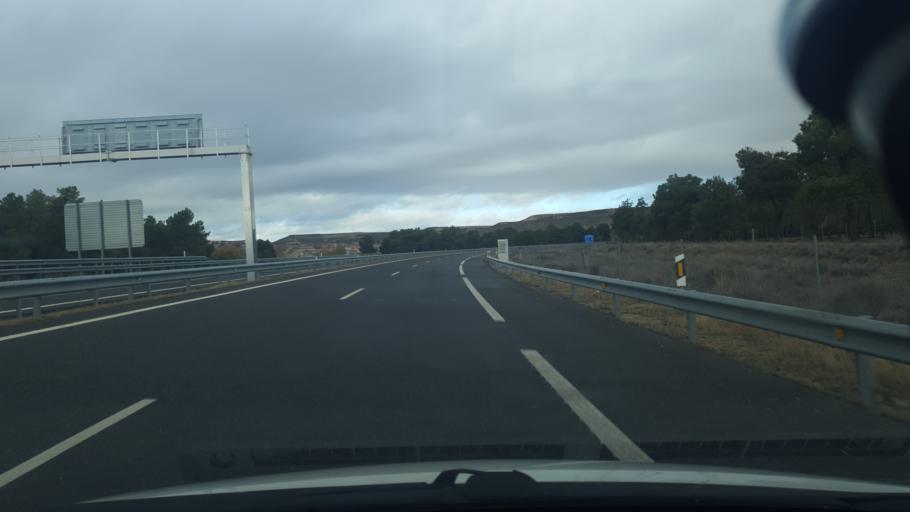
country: ES
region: Castille and Leon
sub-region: Provincia de Segovia
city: Cuellar
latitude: 41.3774
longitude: -4.3010
